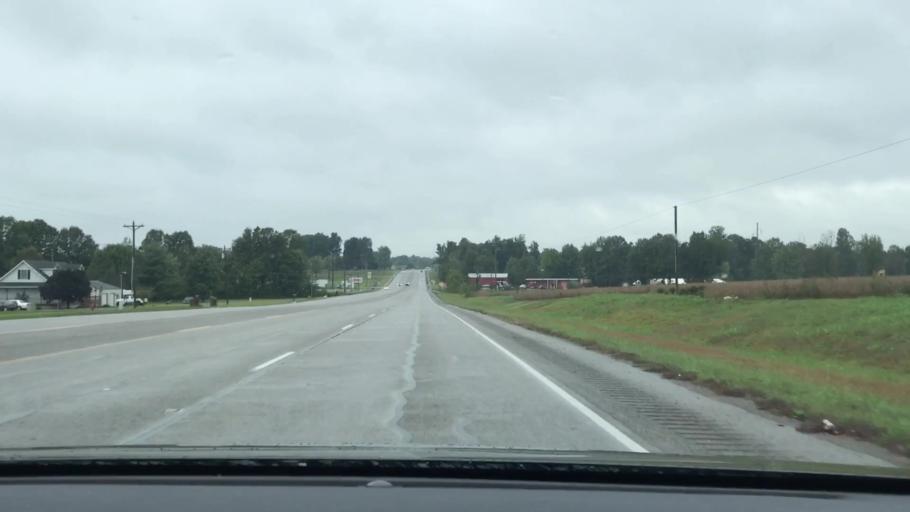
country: US
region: Kentucky
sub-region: Hopkins County
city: Madisonville
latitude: 37.3321
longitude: -87.4269
